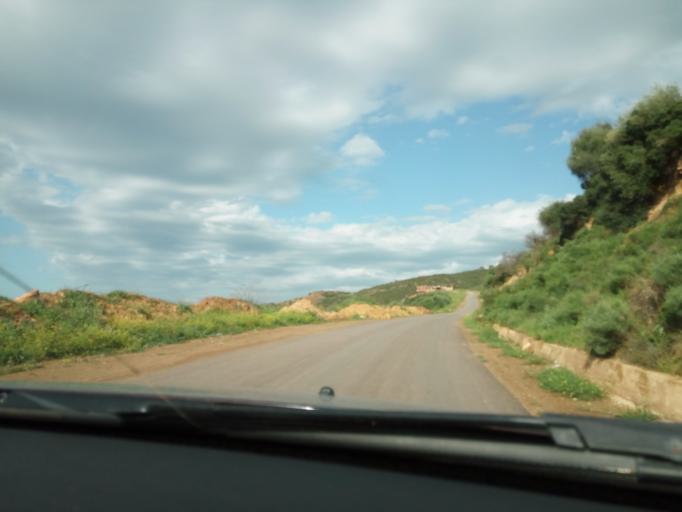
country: DZ
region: Tipaza
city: El Affroun
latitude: 36.3729
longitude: 2.5050
